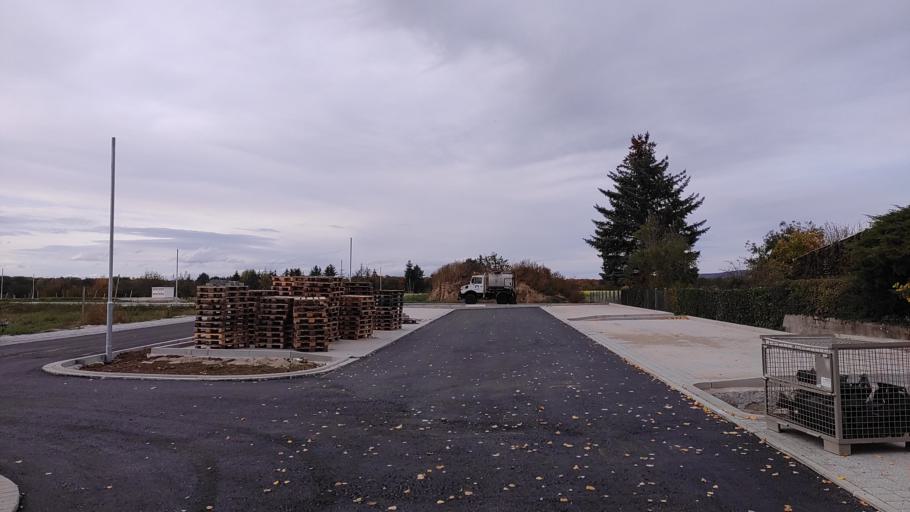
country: DE
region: Baden-Wuerttemberg
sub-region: Freiburg Region
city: Vorstetten
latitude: 48.0836
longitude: 7.8218
